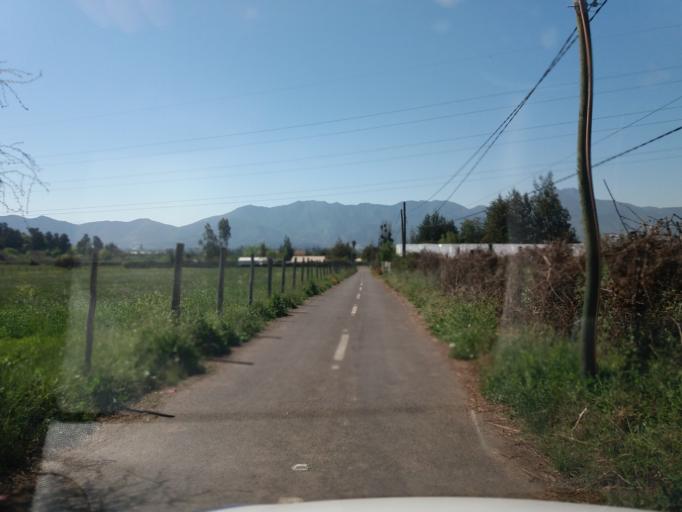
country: CL
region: Valparaiso
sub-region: Provincia de Quillota
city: Quillota
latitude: -32.8583
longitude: -71.2708
